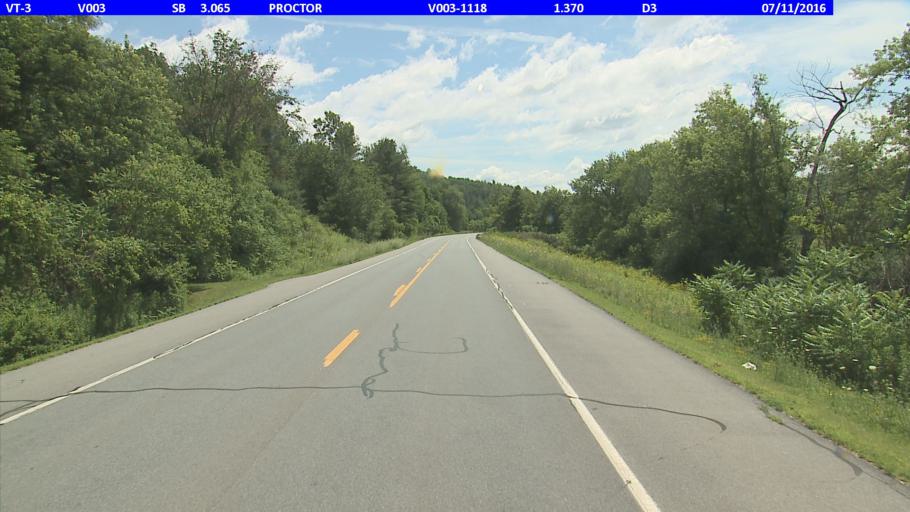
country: US
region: Vermont
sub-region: Rutland County
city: West Rutland
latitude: 43.6437
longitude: -73.0330
